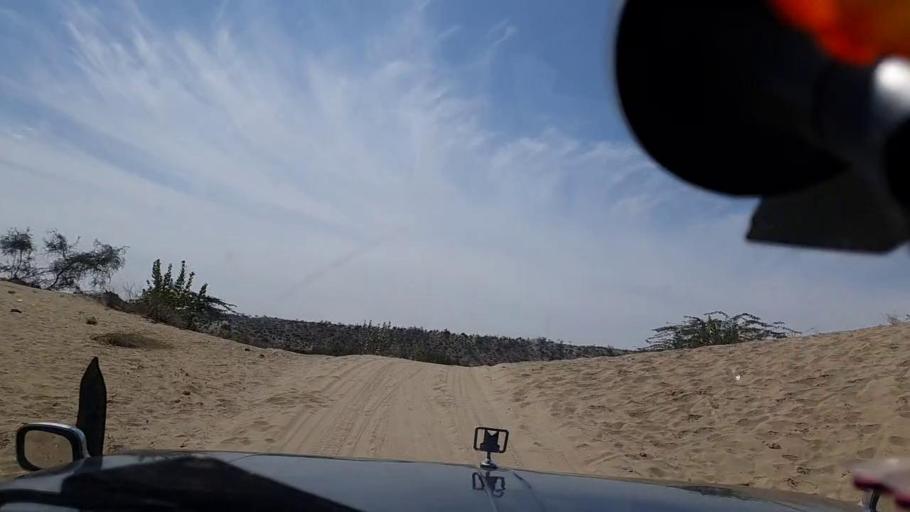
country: PK
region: Sindh
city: Diplo
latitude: 24.3986
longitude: 69.5890
